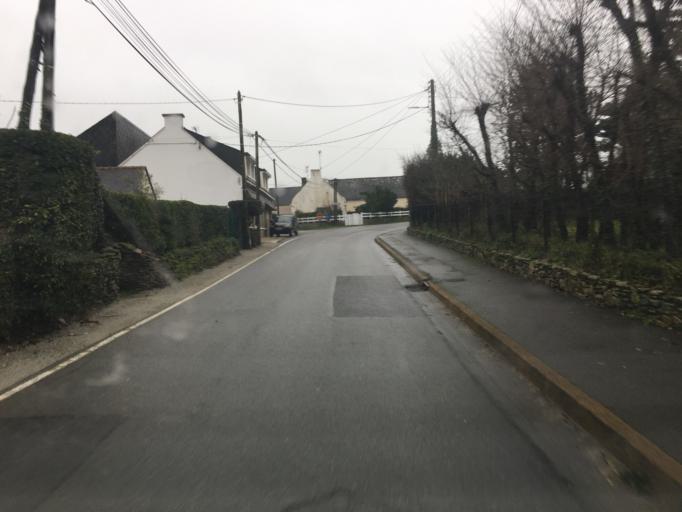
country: FR
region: Brittany
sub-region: Departement du Morbihan
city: Sarzeau
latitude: 47.4997
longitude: -2.6825
